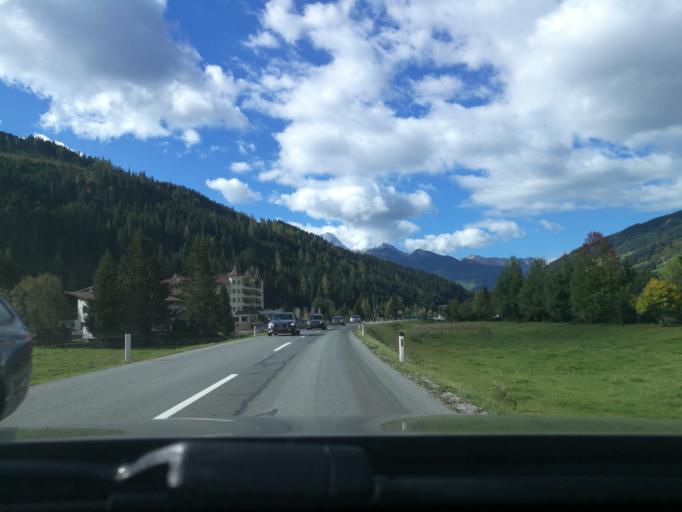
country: AT
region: Tyrol
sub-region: Politischer Bezirk Schwaz
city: Gerlos
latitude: 47.2302
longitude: 12.0524
